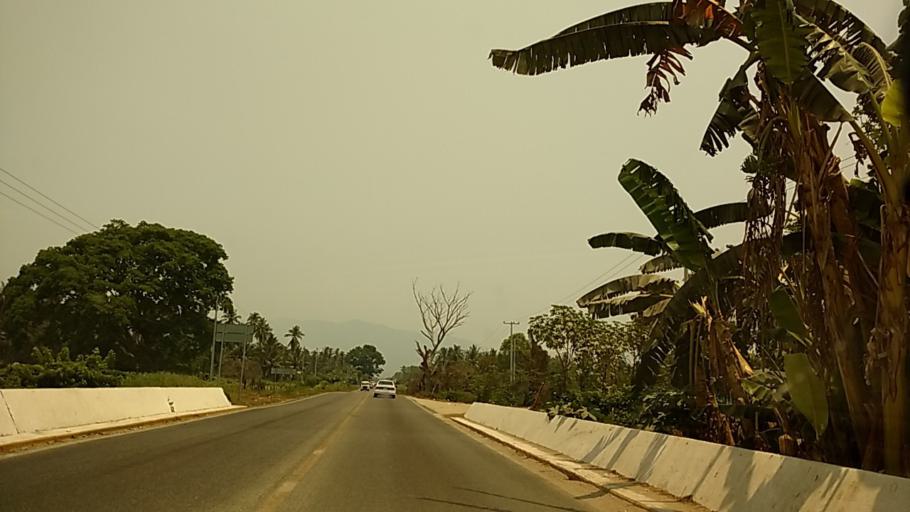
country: MX
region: Guerrero
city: San Jeronimo de Juarez
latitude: 17.1456
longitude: -100.4560
